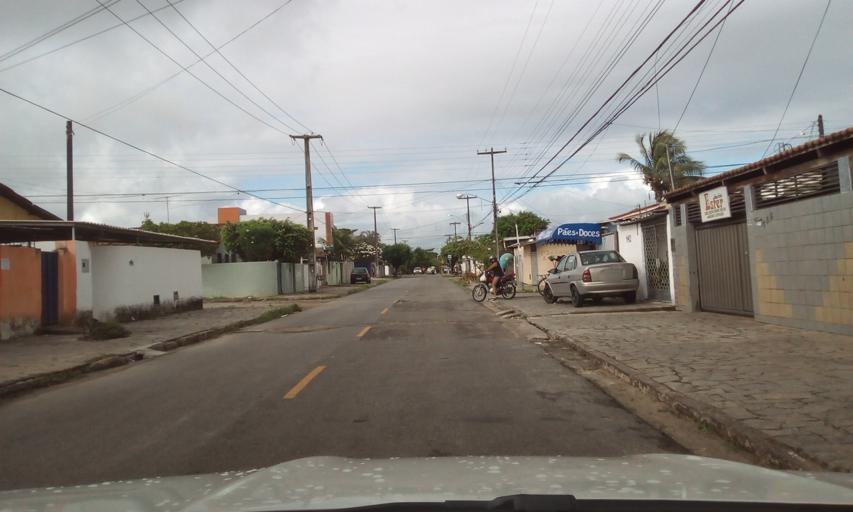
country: BR
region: Paraiba
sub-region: Joao Pessoa
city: Joao Pessoa
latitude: -7.1335
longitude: -34.8513
